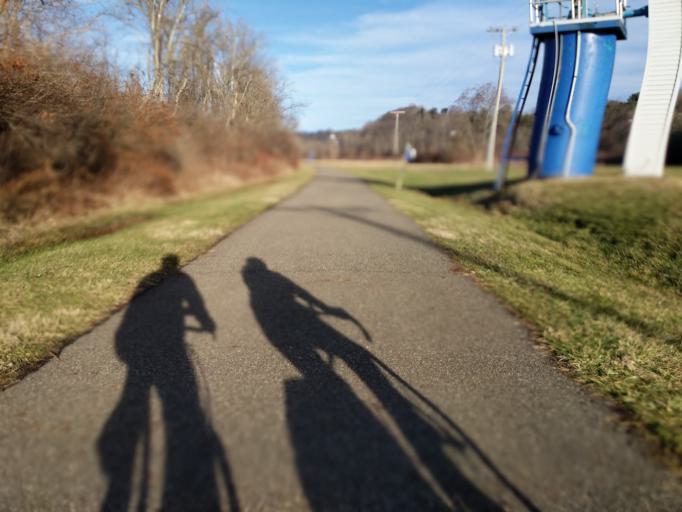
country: US
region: Ohio
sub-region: Athens County
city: Athens
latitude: 39.3379
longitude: -82.1165
